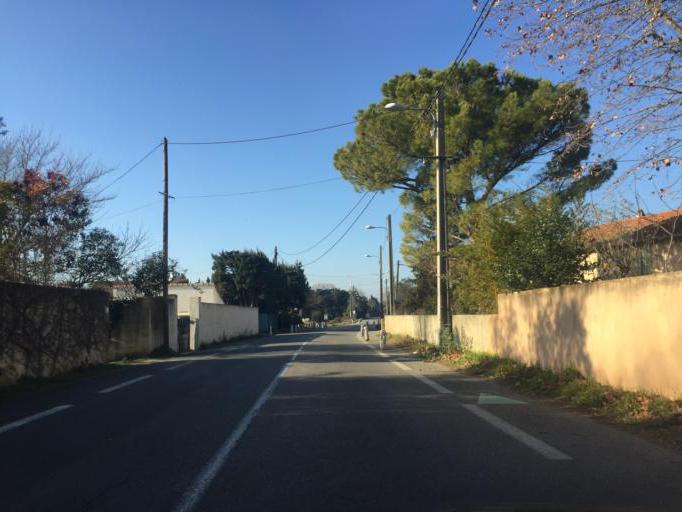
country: FR
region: Provence-Alpes-Cote d'Azur
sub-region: Departement du Vaucluse
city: Montfavet
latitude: 43.9292
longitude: 4.8669
